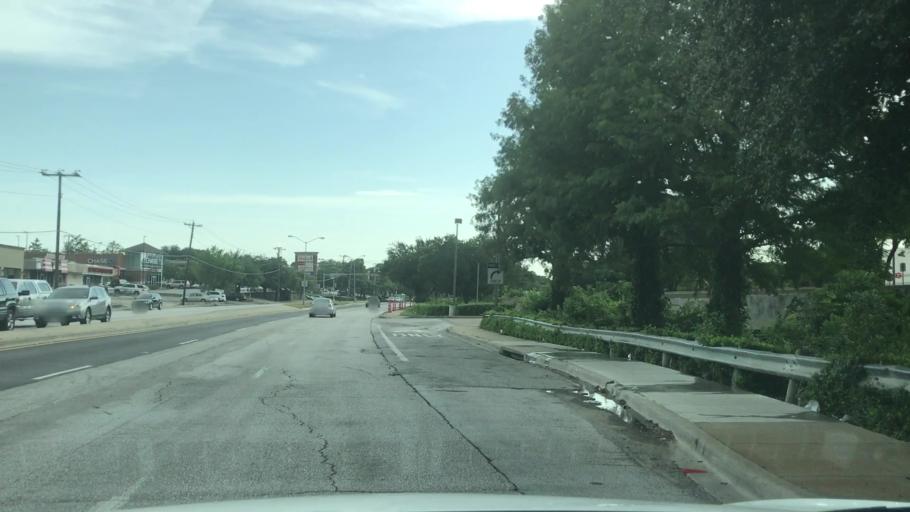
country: US
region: Texas
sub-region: Dallas County
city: Highland Park
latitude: 32.8650
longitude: -96.7440
